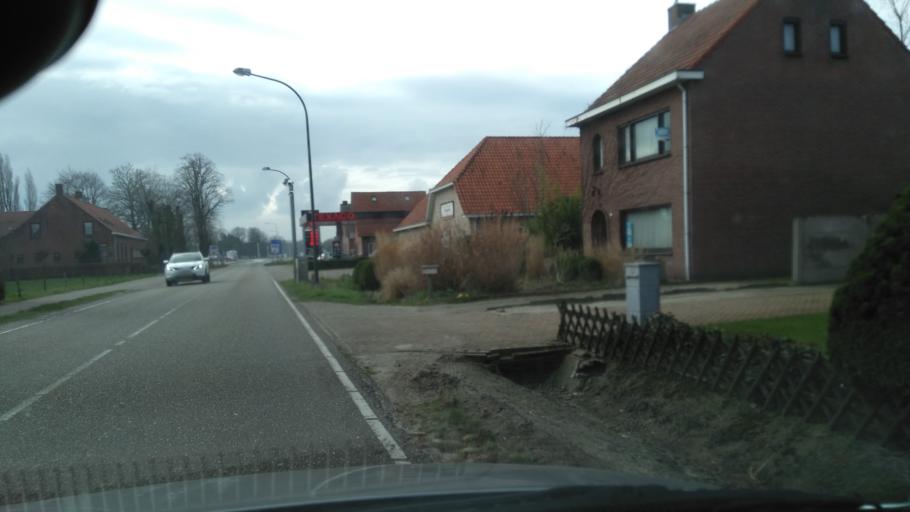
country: NL
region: North Brabant
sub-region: Gemeente Baarle-Nassau
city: Baarle-Nassau
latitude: 51.4317
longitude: 4.9321
